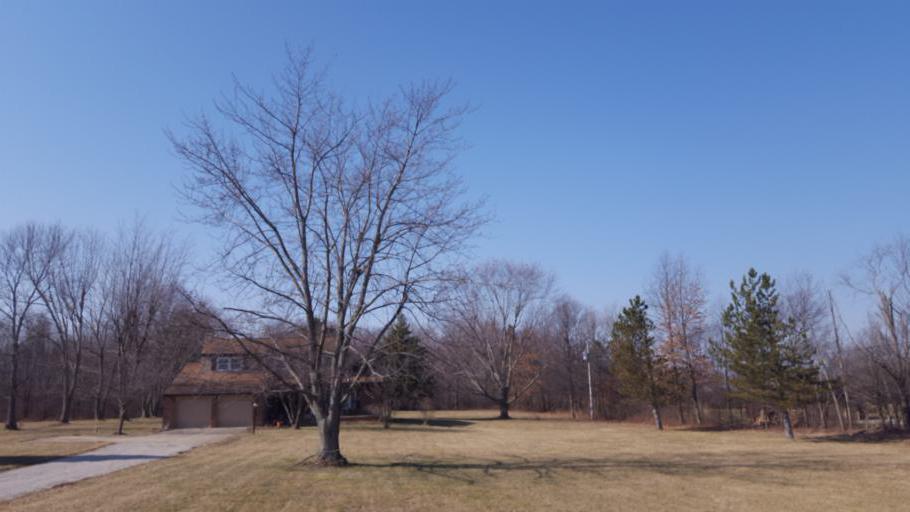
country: US
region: Ohio
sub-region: Richland County
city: Shelby
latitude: 40.8530
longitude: -82.5980
